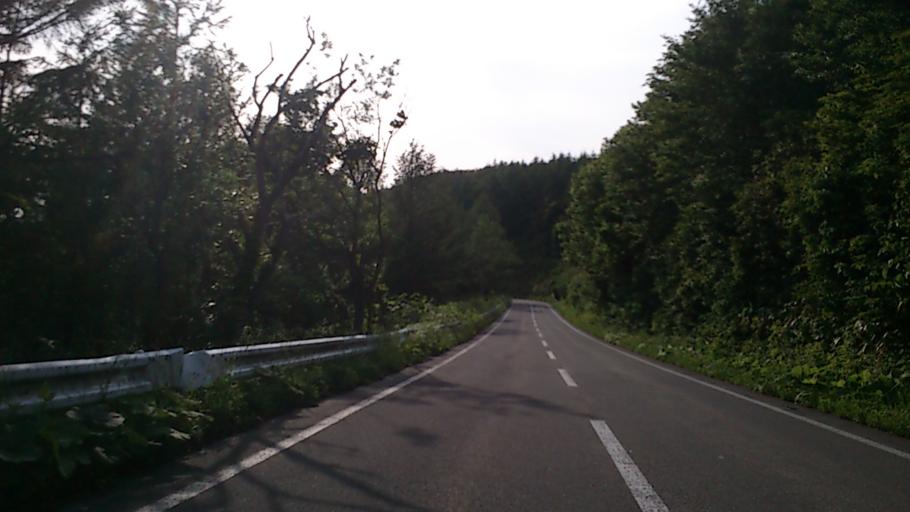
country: JP
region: Aomori
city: Aomori Shi
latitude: 40.6478
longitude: 140.7809
